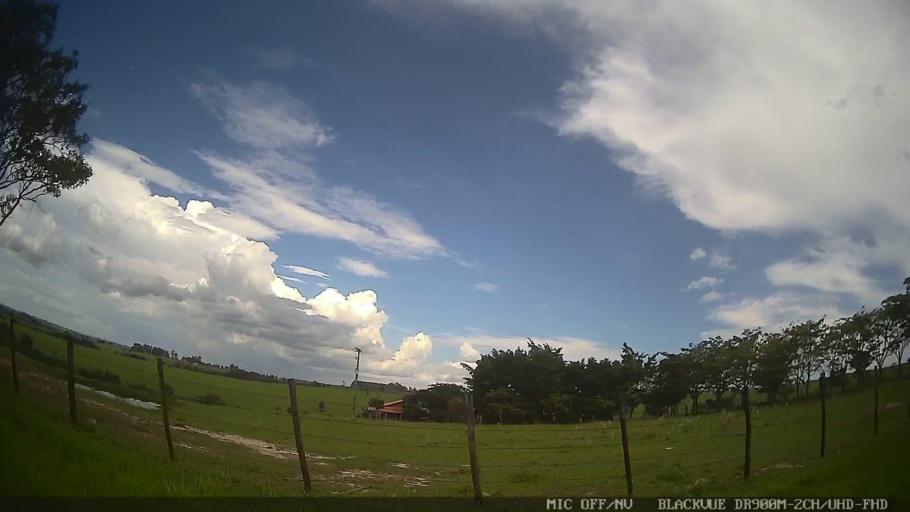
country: BR
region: Sao Paulo
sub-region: Conchas
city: Conchas
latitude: -22.9695
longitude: -47.9848
